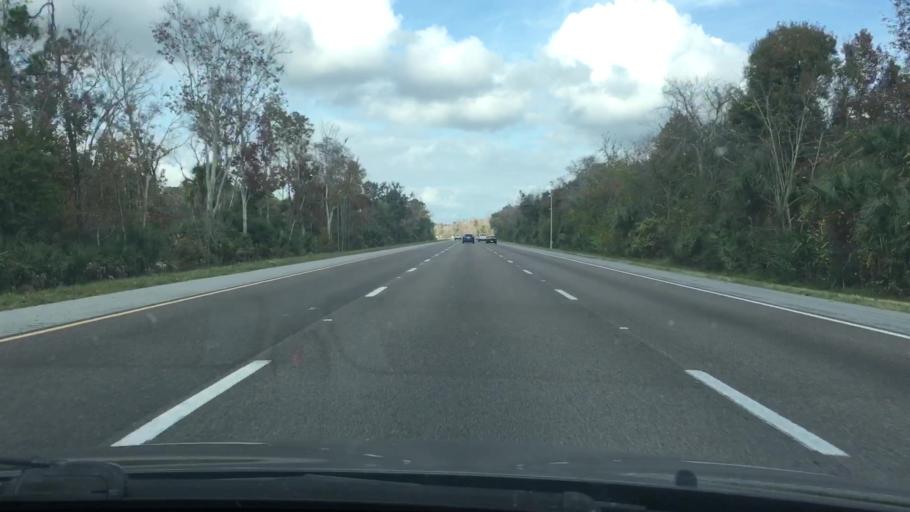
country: US
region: Florida
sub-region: Volusia County
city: Oak Hill
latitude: 28.8658
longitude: -80.9185
